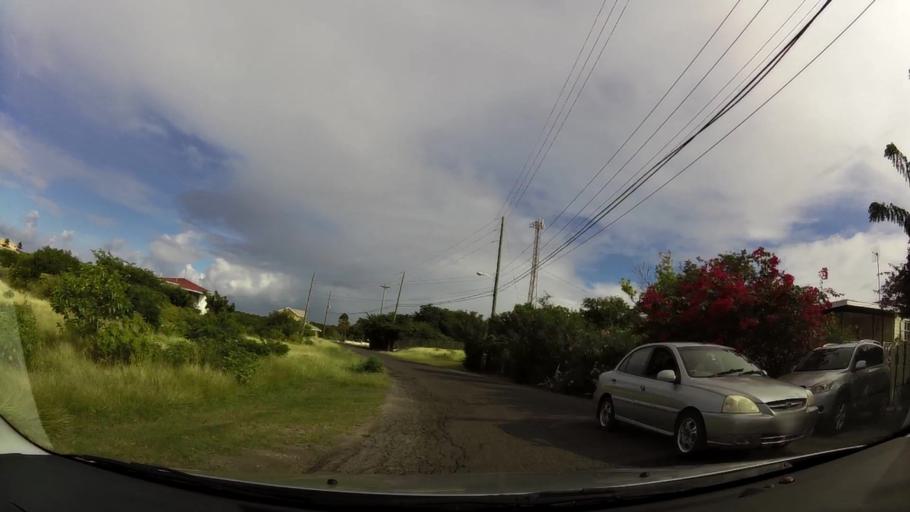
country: AG
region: Saint Peter
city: Parham
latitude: 17.0895
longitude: -61.7004
